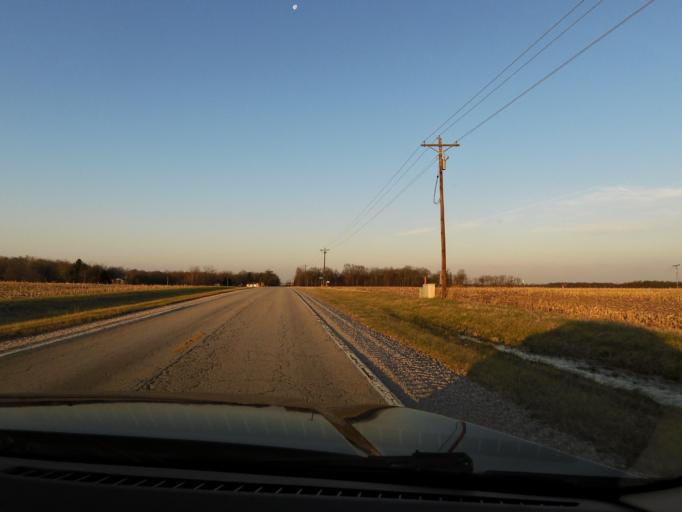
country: US
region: Illinois
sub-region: Marion County
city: Salem
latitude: 38.7653
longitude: -88.9755
